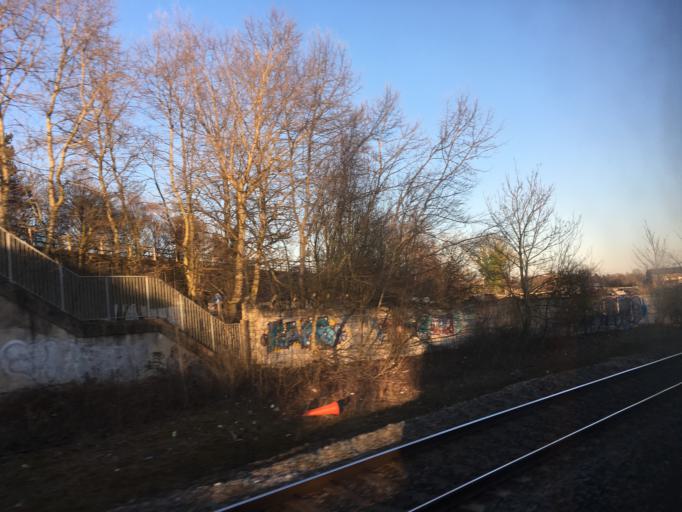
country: GB
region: England
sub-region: Derbyshire
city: Borrowash
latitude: 52.9143
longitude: -1.4216
